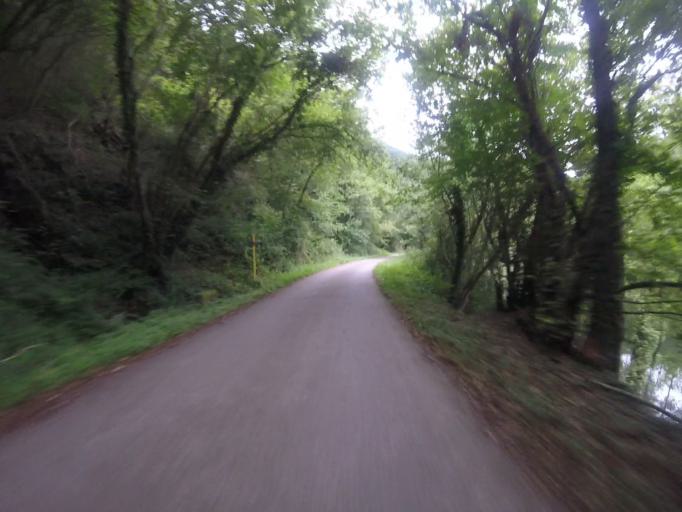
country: ES
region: Navarre
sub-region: Provincia de Navarra
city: Igantzi
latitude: 43.2180
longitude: -1.6797
